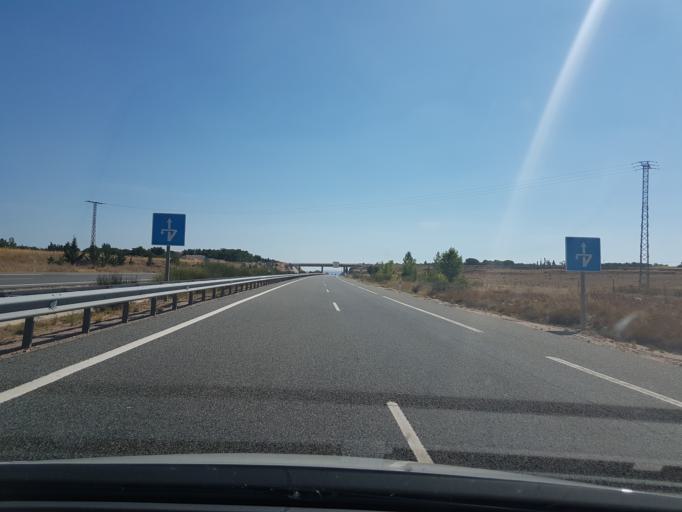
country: ES
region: Castille and Leon
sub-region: Provincia de Avila
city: Cardenosa
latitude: 40.7026
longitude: -4.7424
